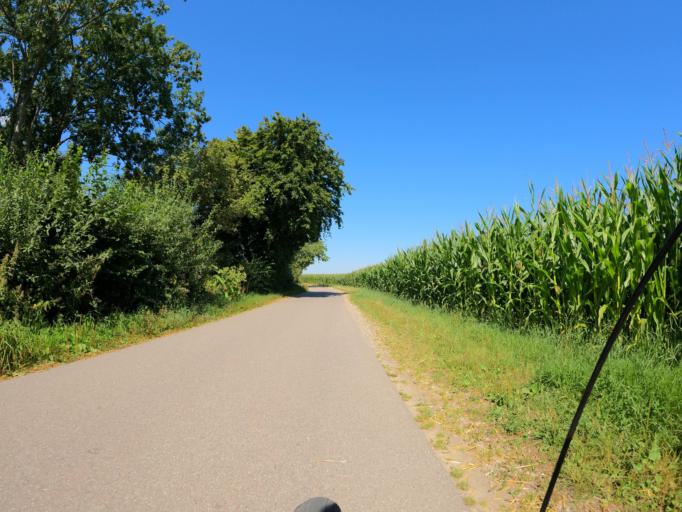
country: DE
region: Schleswig-Holstein
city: Steinbergkirche
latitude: 54.7751
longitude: 9.7618
